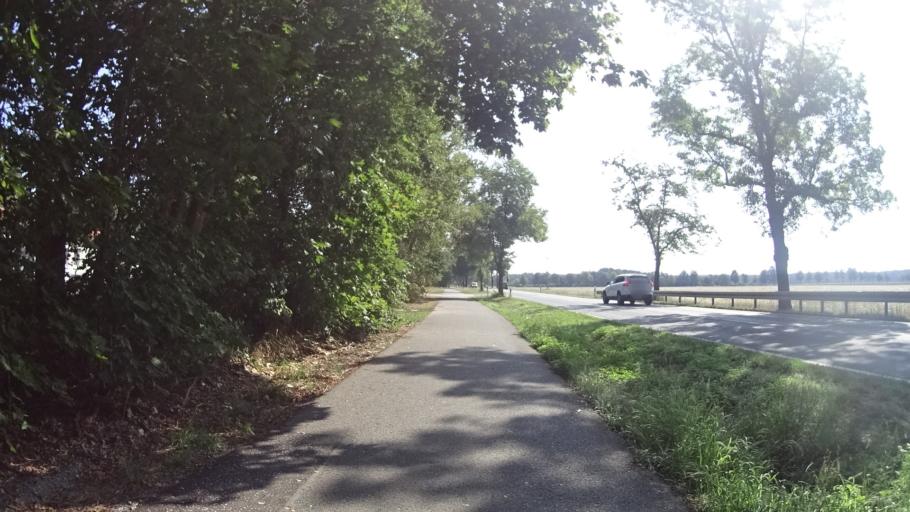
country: DE
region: Brandenburg
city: Guhrow
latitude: 51.8089
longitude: 14.2151
